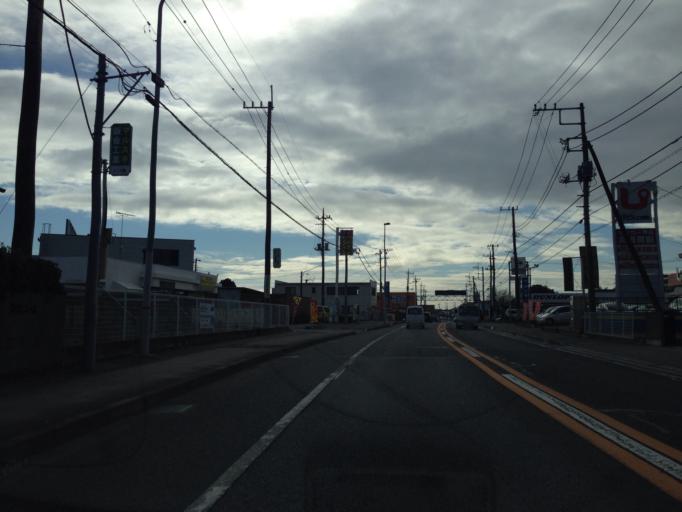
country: JP
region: Ibaraki
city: Naka
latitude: 36.0179
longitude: 140.1588
